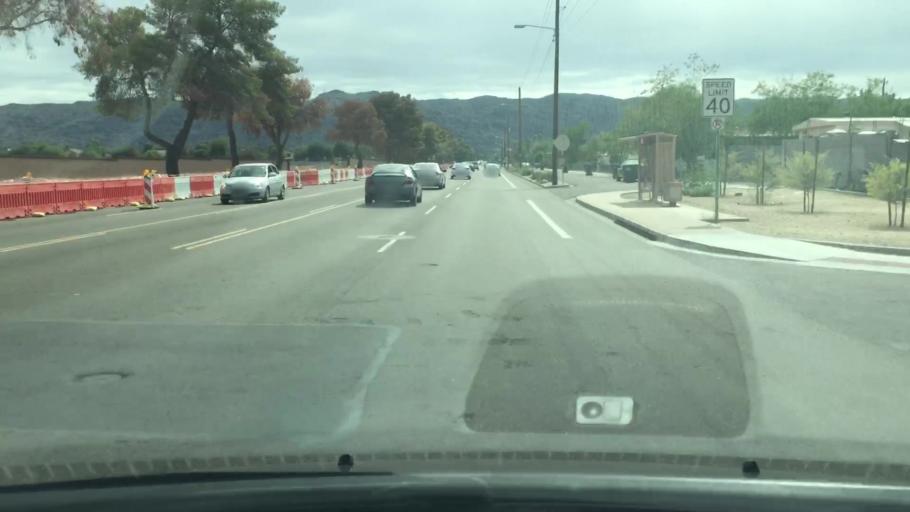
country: US
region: Arizona
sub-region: Maricopa County
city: Guadalupe
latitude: 33.3898
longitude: -112.0302
